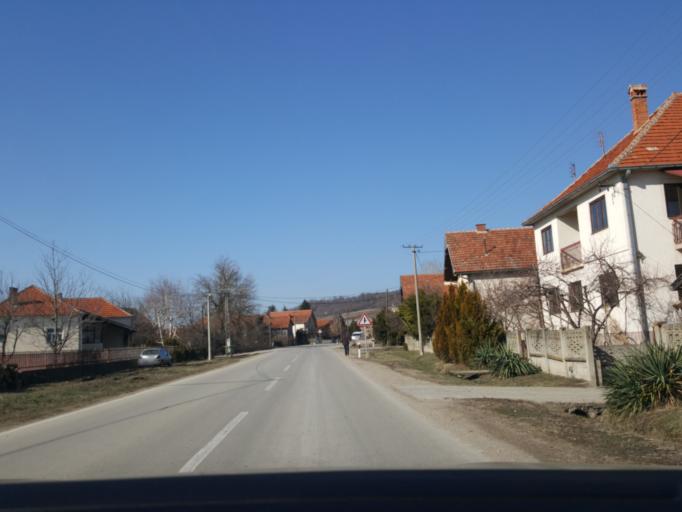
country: RS
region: Central Serbia
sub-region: Nisavski Okrug
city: Aleksinac
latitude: 43.4493
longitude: 21.7967
